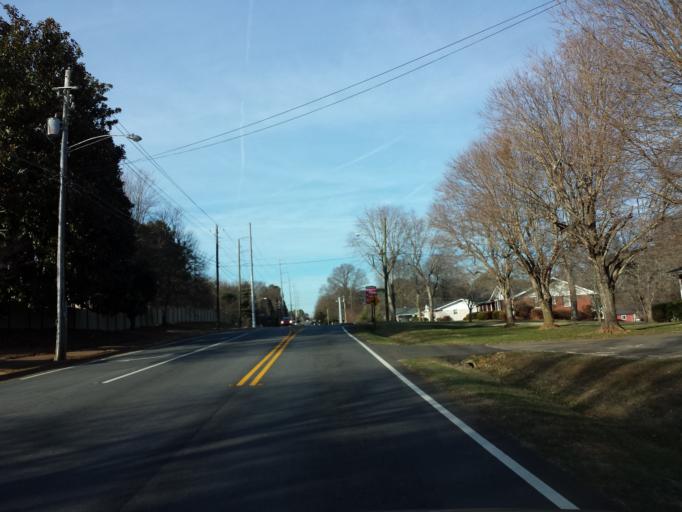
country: US
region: Georgia
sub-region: Cobb County
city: Kennesaw
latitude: 34.0273
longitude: -84.5497
